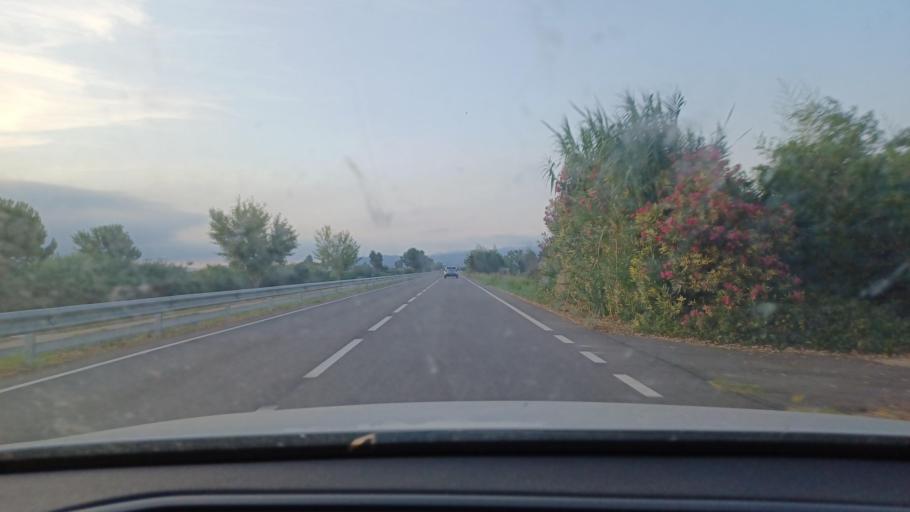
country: ES
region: Catalonia
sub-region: Provincia de Tarragona
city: Amposta
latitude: 40.6740
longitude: 0.5906
